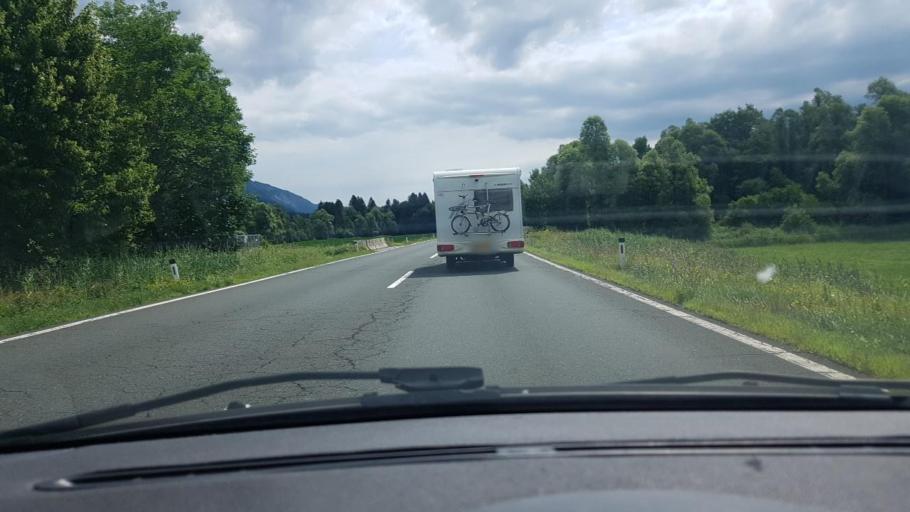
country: AT
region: Carinthia
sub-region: Politischer Bezirk Villach Land
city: Feistritz an der Gail
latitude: 46.5761
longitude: 13.6366
